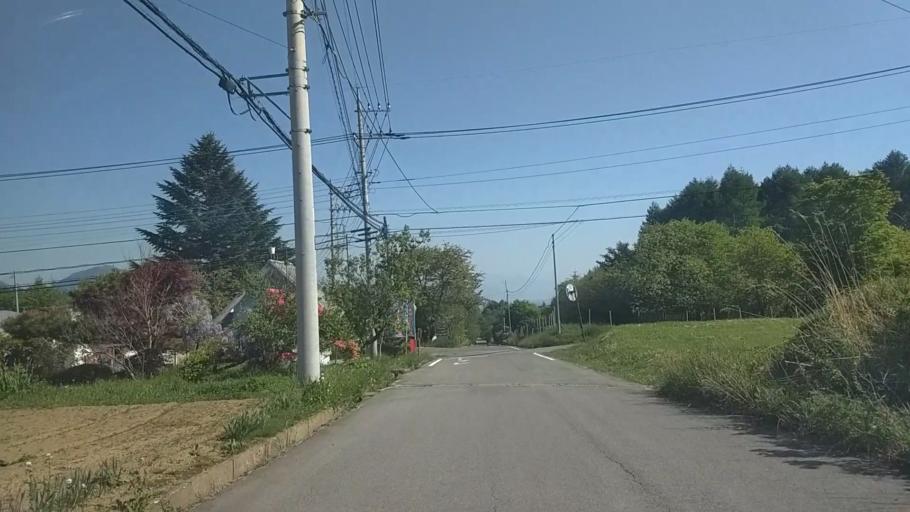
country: JP
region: Yamanashi
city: Nirasaki
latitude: 35.8952
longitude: 138.4113
